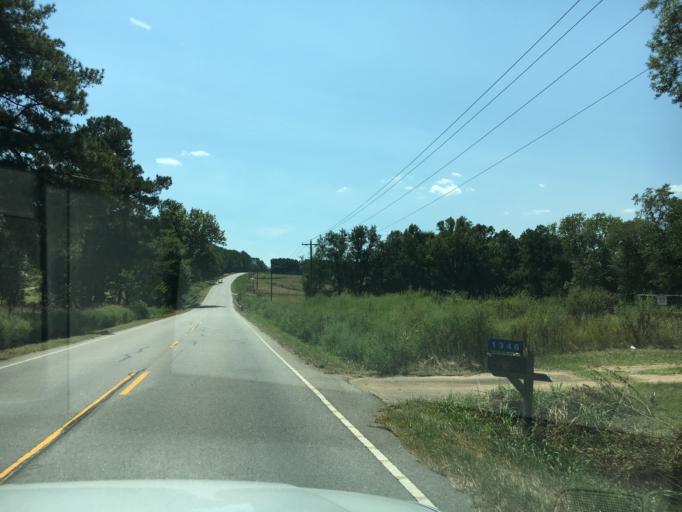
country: US
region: South Carolina
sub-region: Saluda County
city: Saluda
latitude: 33.9126
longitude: -81.7043
